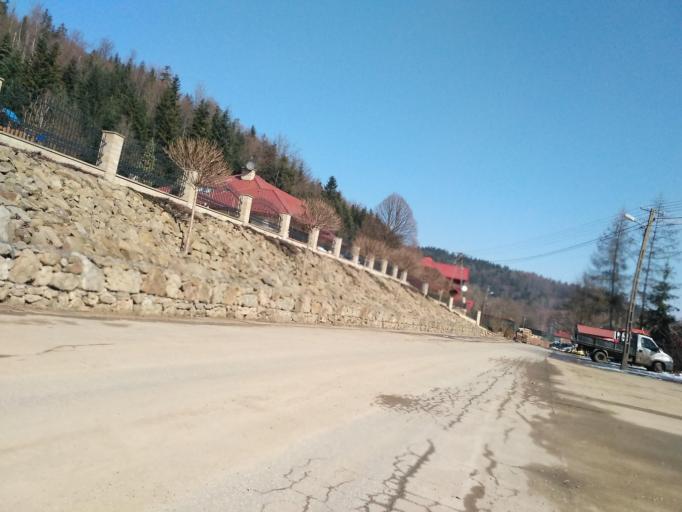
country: PL
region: Subcarpathian Voivodeship
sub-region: Powiat brzozowski
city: Jablonica Polska
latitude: 49.7515
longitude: 21.8663
